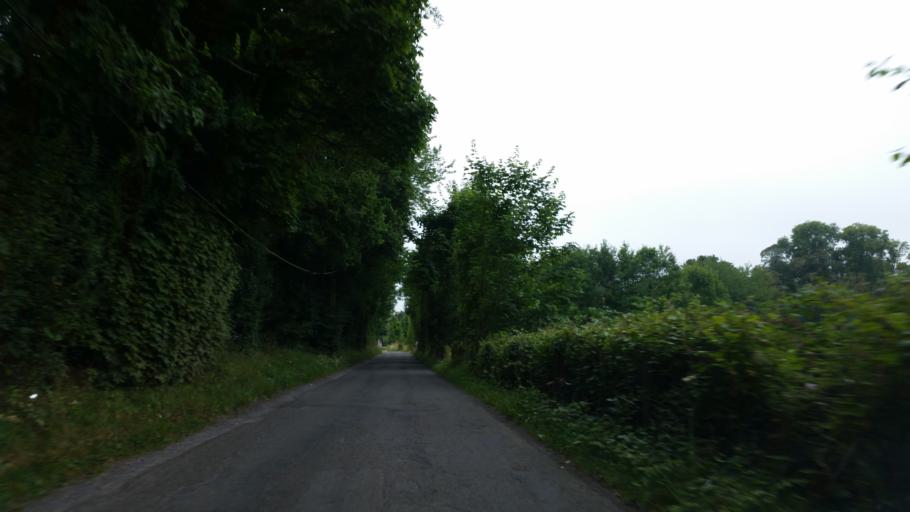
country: FR
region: Lower Normandy
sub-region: Departement du Calvados
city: Honfleur
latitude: 49.3890
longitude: 0.2429
